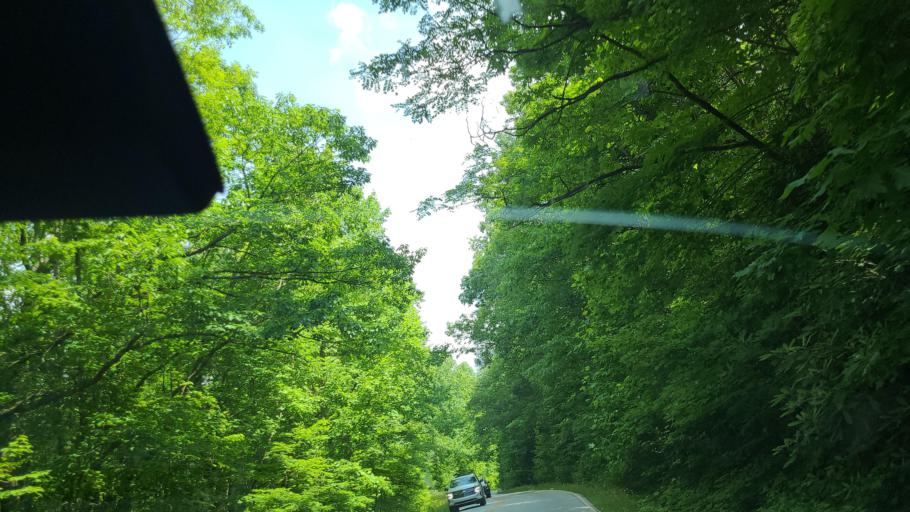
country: US
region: Georgia
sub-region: Rabun County
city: Mountain City
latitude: 35.0186
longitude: -83.1871
